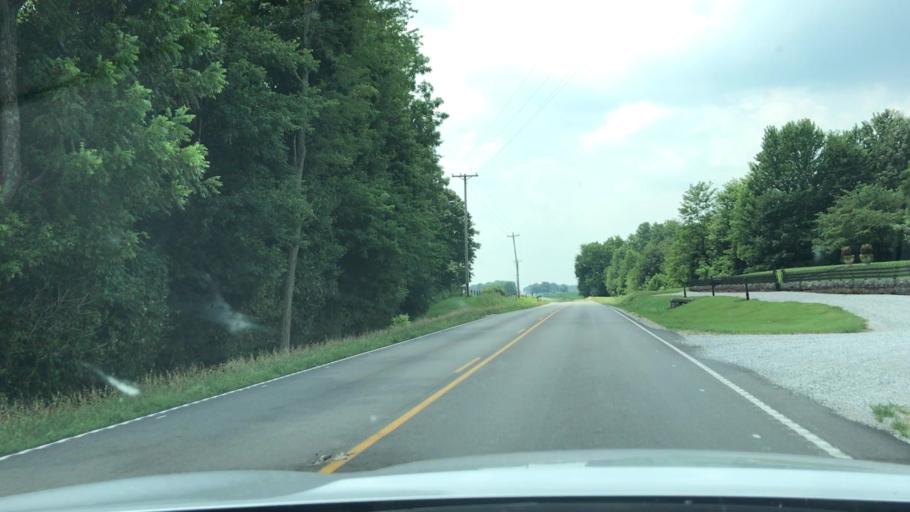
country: US
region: Kentucky
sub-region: Todd County
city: Guthrie
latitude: 36.7069
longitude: -87.1066
